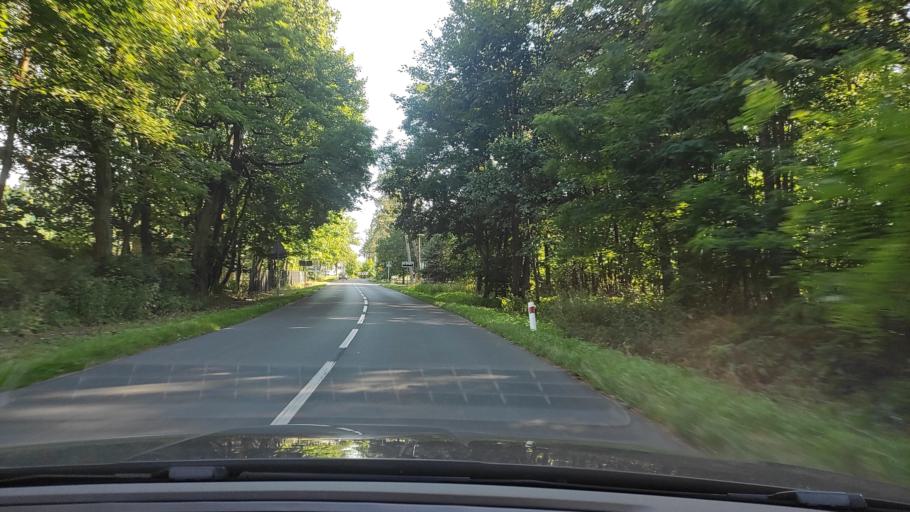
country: PL
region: Greater Poland Voivodeship
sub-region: Powiat poznanski
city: Kobylnica
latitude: 52.4481
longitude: 17.0772
